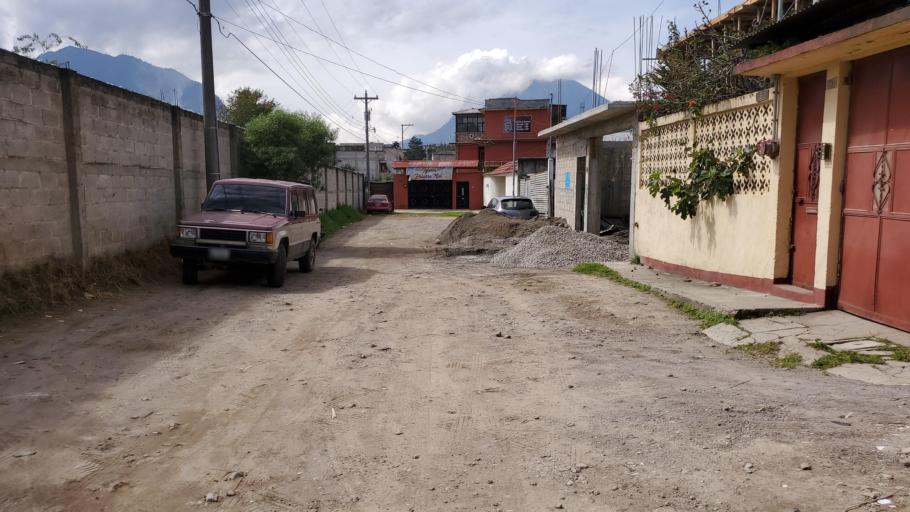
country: GT
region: Quetzaltenango
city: Quetzaltenango
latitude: 14.8382
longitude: -91.5395
